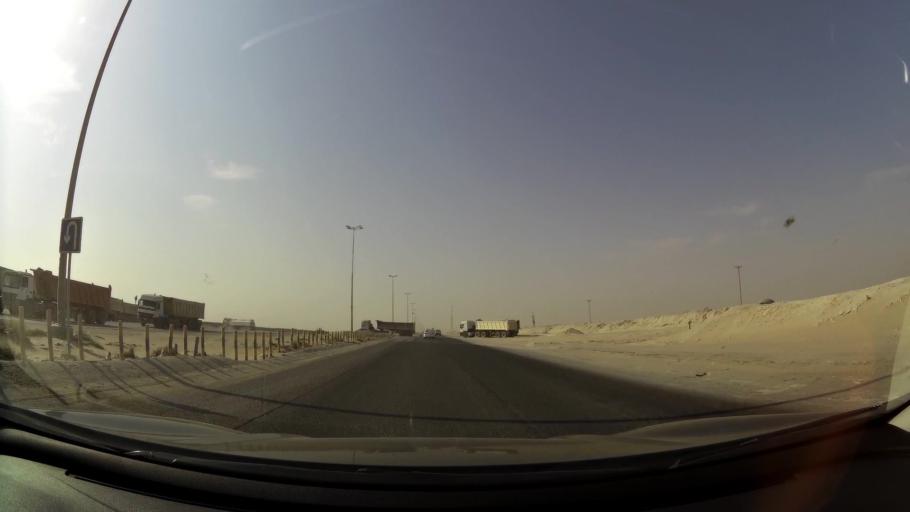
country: KW
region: Al Ahmadi
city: Al Ahmadi
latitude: 28.9143
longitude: 48.0982
